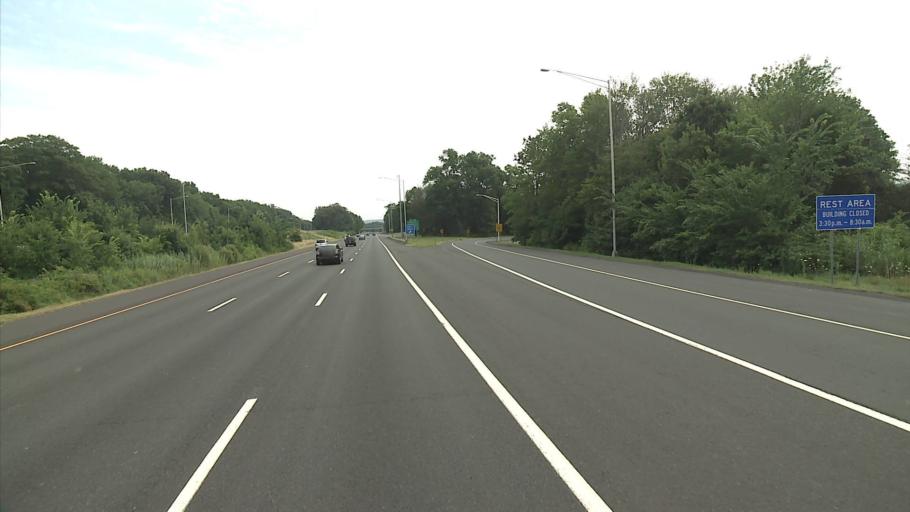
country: US
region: Connecticut
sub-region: New Haven County
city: Cheshire Village
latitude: 41.5739
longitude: -72.9053
